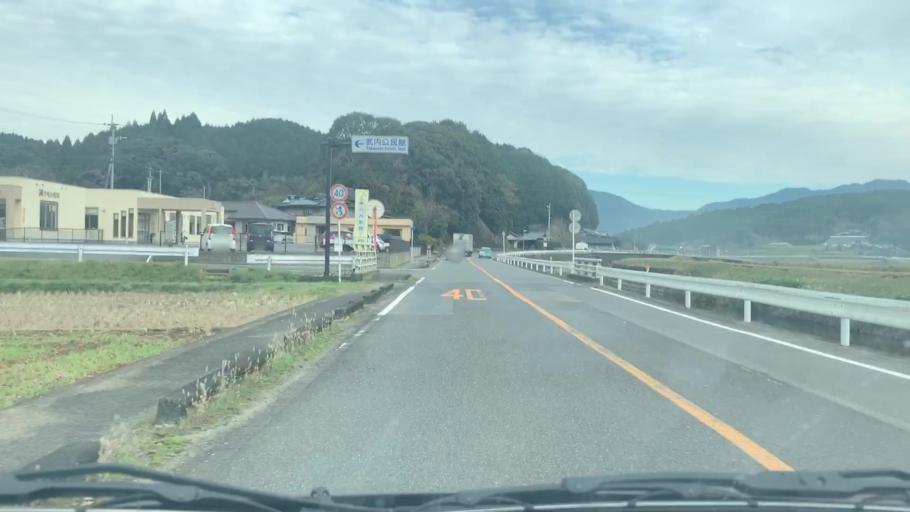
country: JP
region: Saga Prefecture
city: Takeocho-takeo
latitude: 33.2294
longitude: 129.9641
